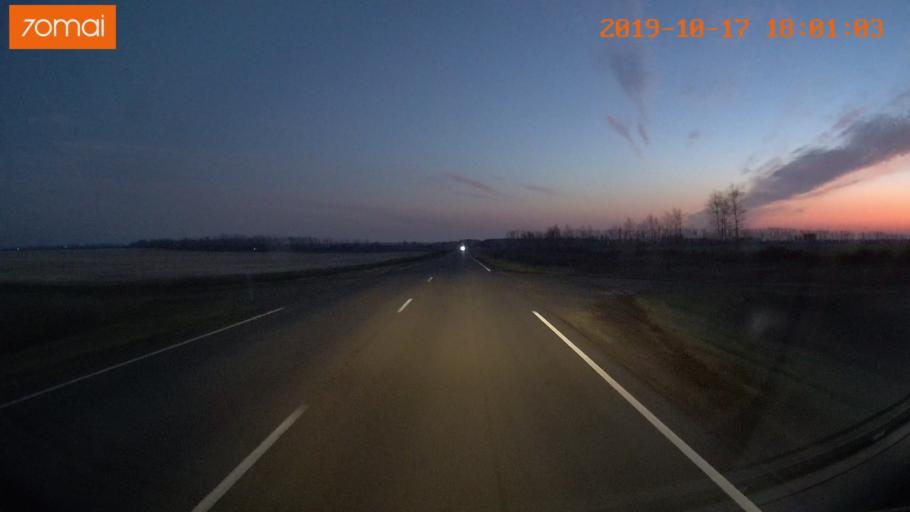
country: RU
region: Tula
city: Kurkino
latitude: 53.5136
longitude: 38.6121
